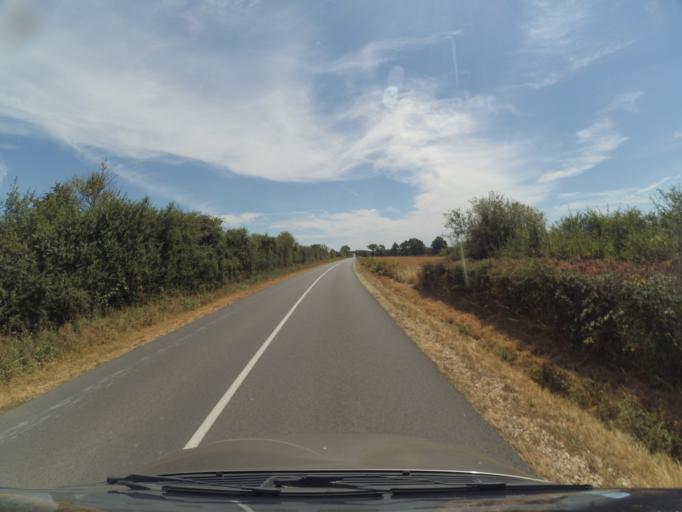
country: FR
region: Poitou-Charentes
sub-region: Departement de la Vienne
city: Availles-Limouzine
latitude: 46.1451
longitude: 0.5557
